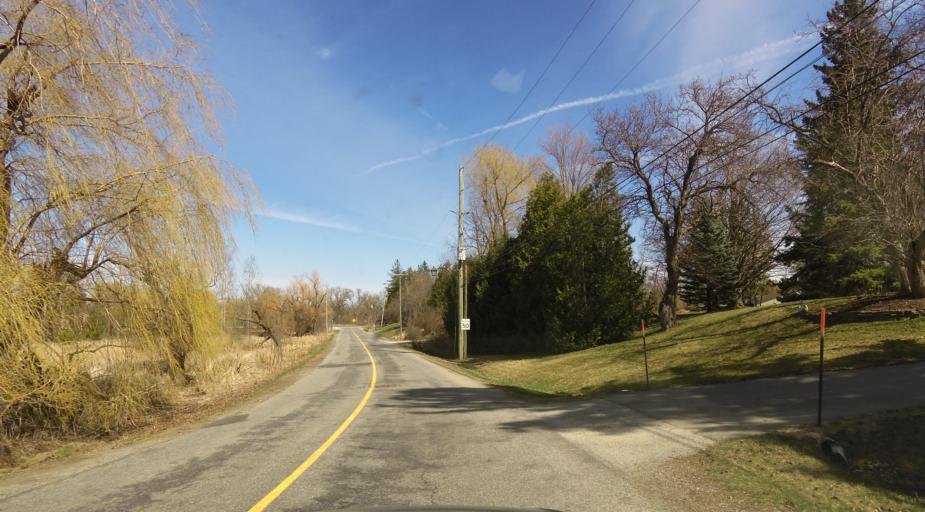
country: CA
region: Ontario
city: Brampton
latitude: 43.6321
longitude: -79.7616
